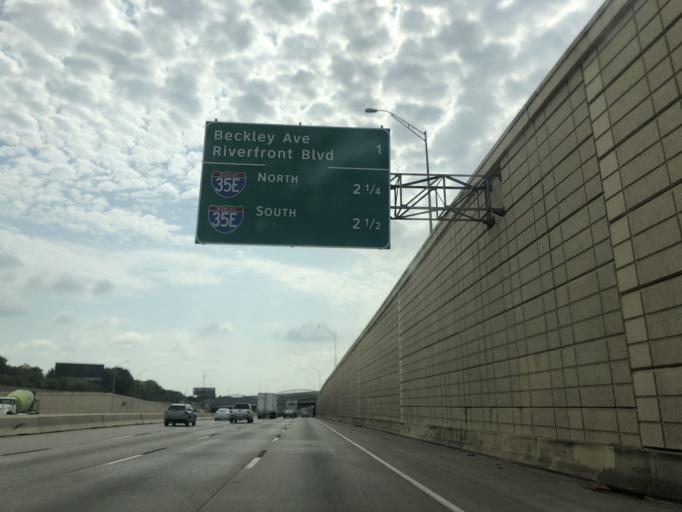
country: US
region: Texas
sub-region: Dallas County
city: Cockrell Hill
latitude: 32.7653
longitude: -96.8536
